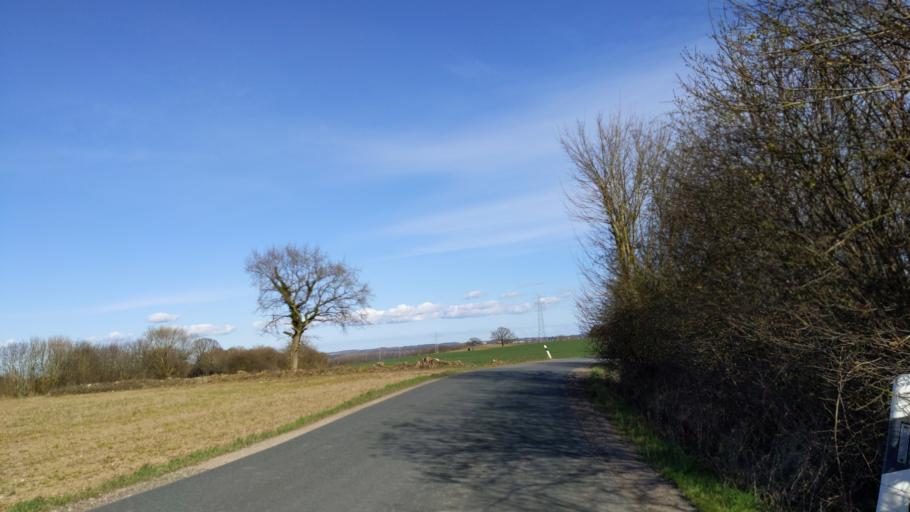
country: DE
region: Schleswig-Holstein
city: Sierksdorf
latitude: 54.1053
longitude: 10.7505
